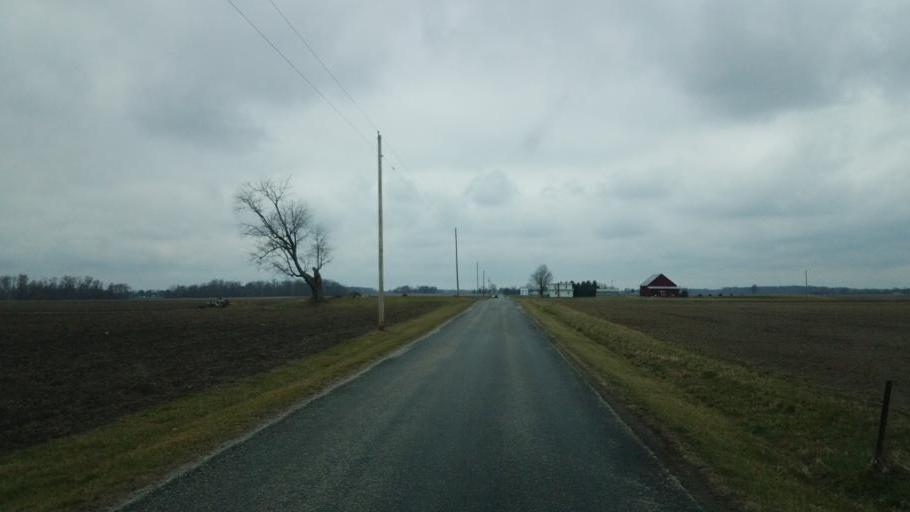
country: US
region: Ohio
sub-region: Delaware County
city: Ashley
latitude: 40.3840
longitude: -82.9924
